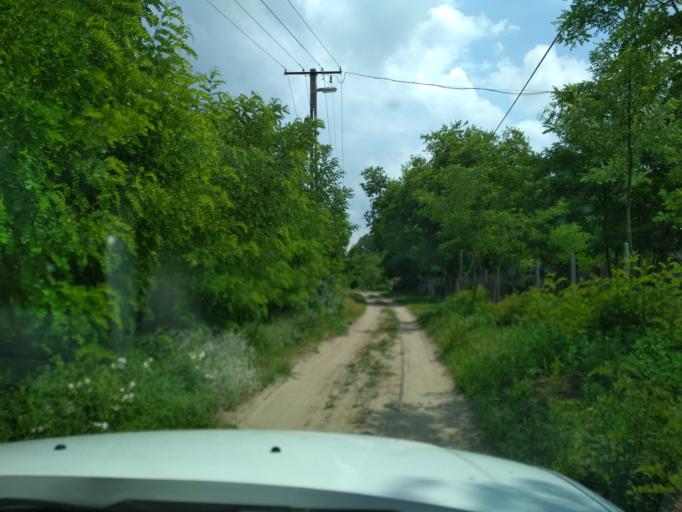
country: HU
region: Pest
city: Tapioszentmarton
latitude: 47.3665
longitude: 19.7710
